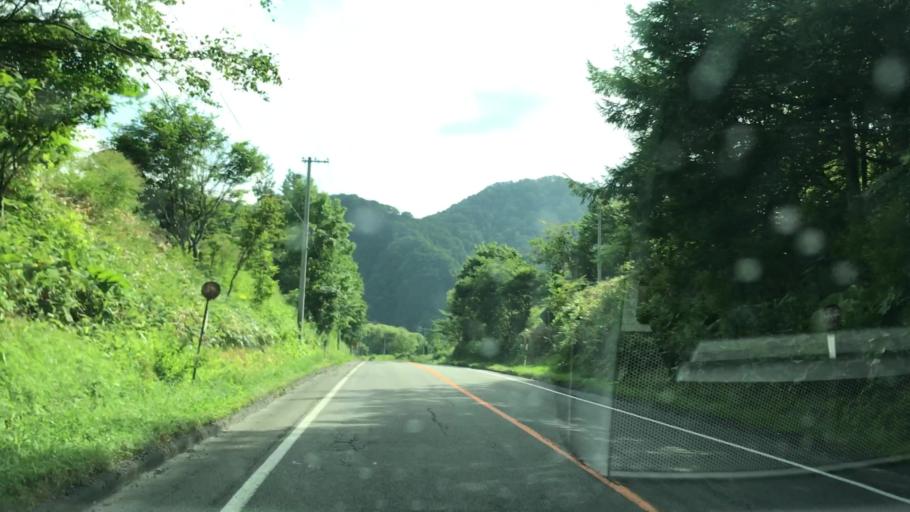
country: JP
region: Hokkaido
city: Shizunai-furukawacho
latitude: 42.7995
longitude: 142.3971
